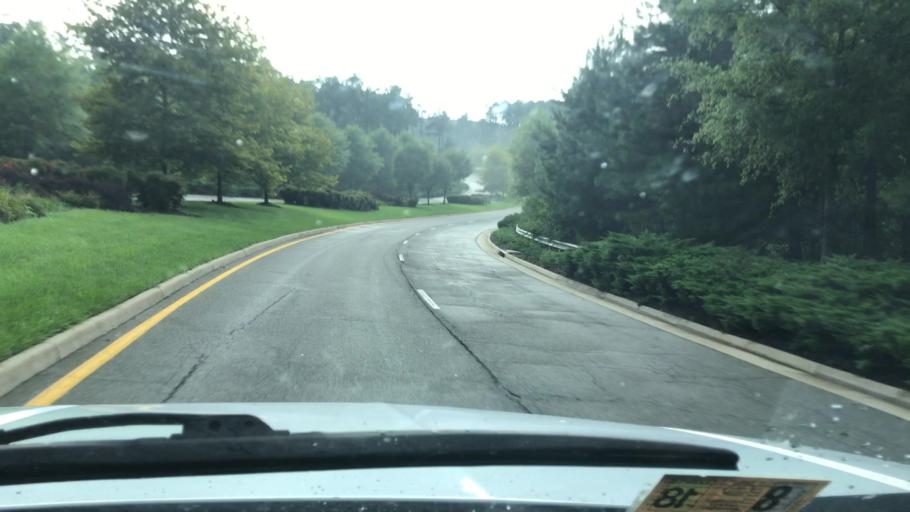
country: US
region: Virginia
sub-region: Henrico County
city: Short Pump
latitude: 37.6368
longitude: -77.6735
